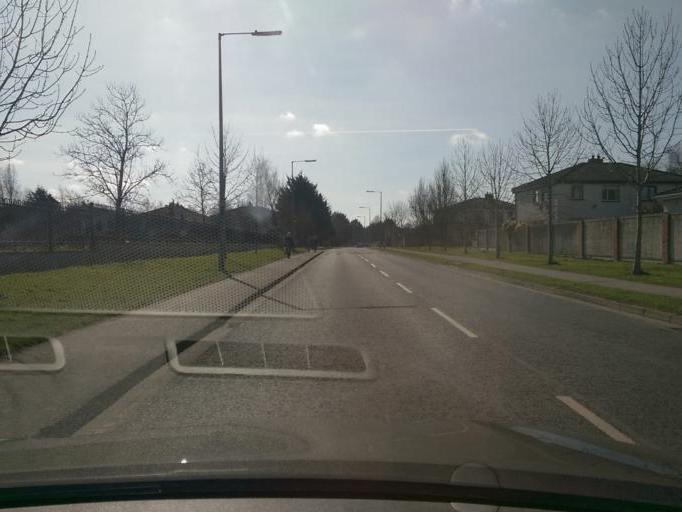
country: IE
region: Leinster
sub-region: Kildare
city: Maynooth
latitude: 53.3742
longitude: -6.5970
